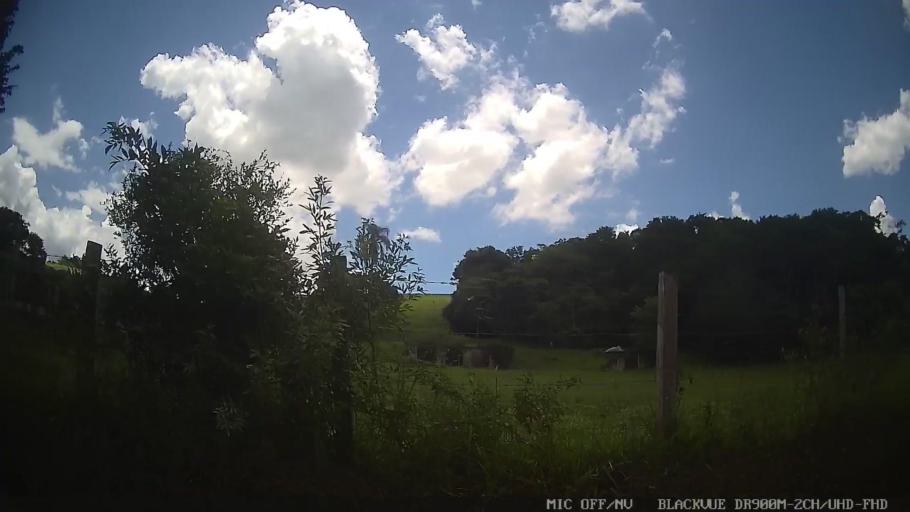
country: BR
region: Sao Paulo
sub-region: Braganca Paulista
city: Braganca Paulista
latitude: -23.0157
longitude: -46.4684
